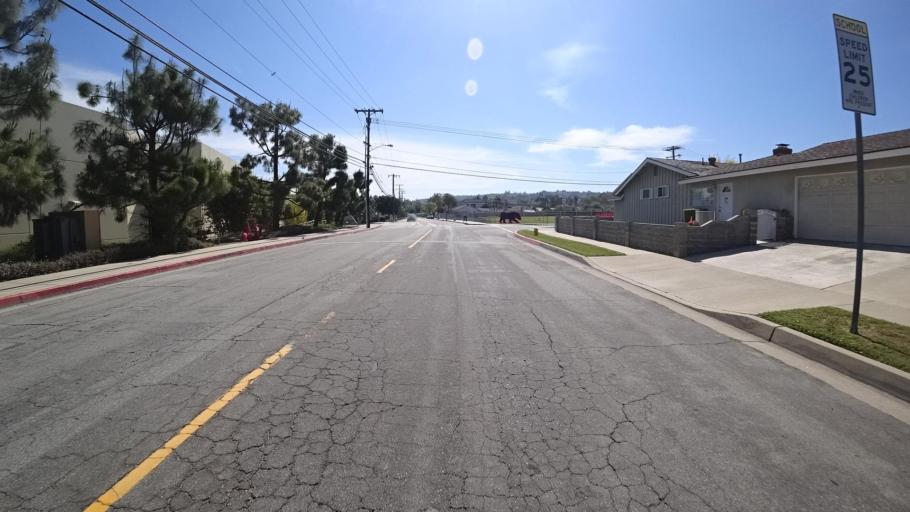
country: US
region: California
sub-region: Los Angeles County
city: Walnut
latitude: 33.9933
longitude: -117.8733
